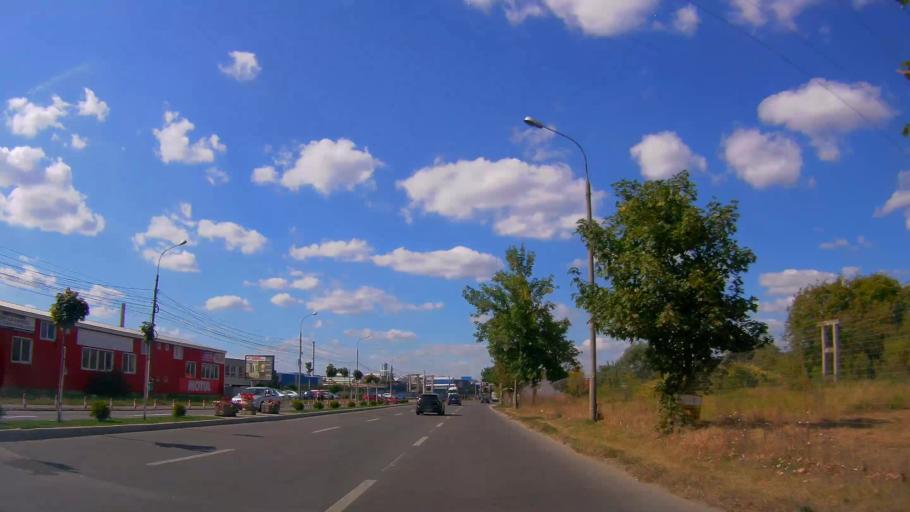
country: RO
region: Salaj
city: Zalau
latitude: 47.2057
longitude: 23.0479
